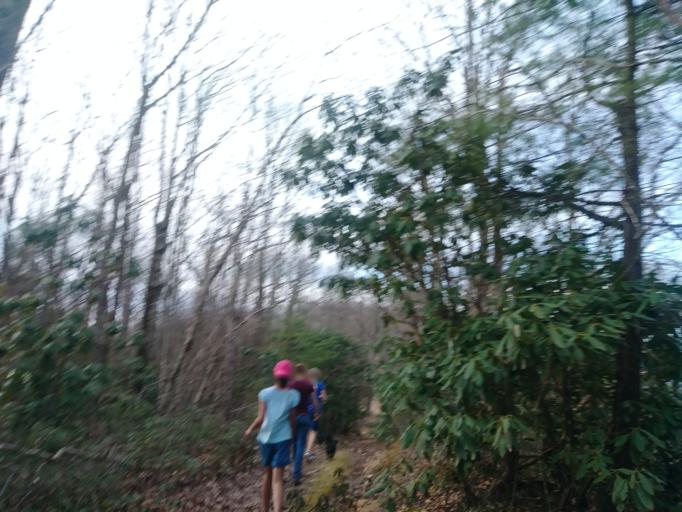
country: US
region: Tennessee
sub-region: Greene County
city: Tusculum
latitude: 36.0554
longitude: -82.6729
